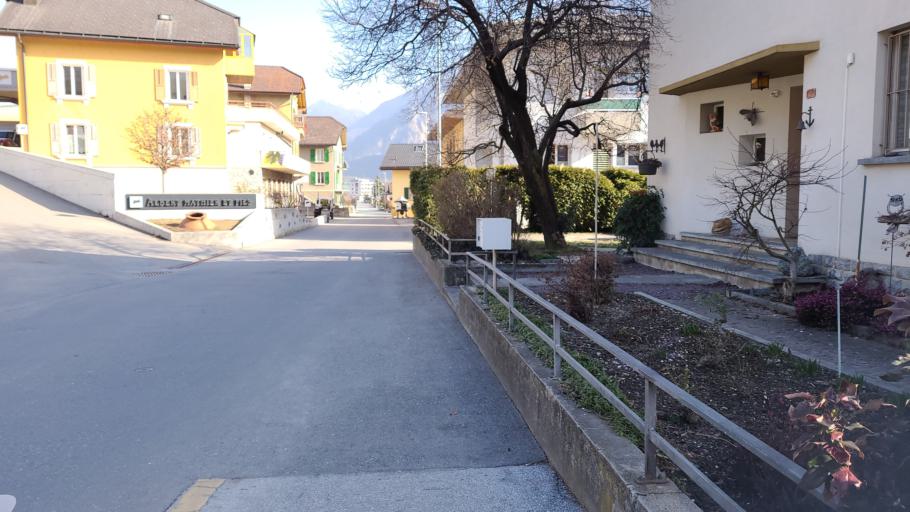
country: CH
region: Valais
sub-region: Leuk District
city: Salgesch
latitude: 46.3113
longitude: 7.5718
